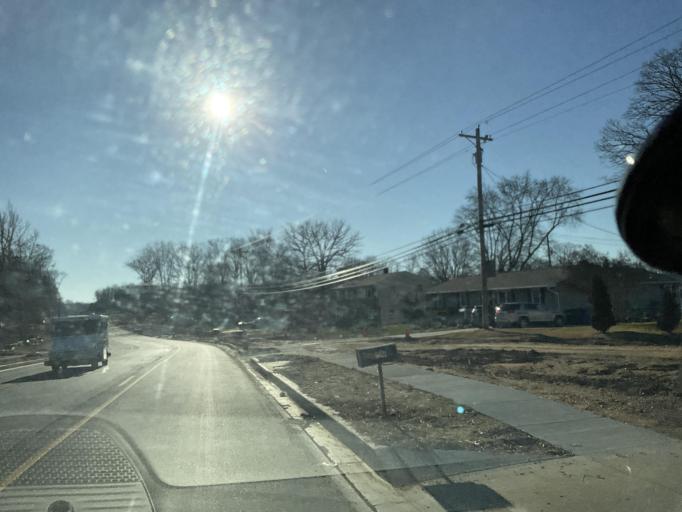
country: US
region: Maryland
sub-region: Charles County
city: Bryans Road
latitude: 38.6336
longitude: -77.0792
